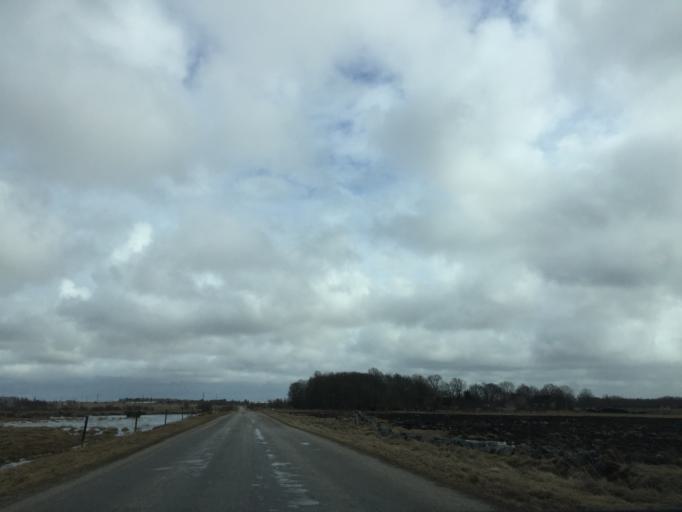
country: EE
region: Laeaene
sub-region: Lihula vald
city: Lihula
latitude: 58.7278
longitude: 23.8957
